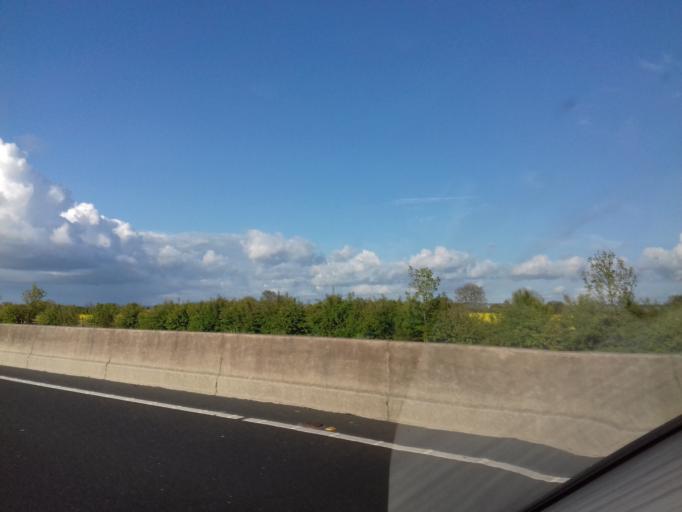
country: IE
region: Leinster
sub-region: County Carlow
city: Bagenalstown
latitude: 52.7393
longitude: -6.9978
